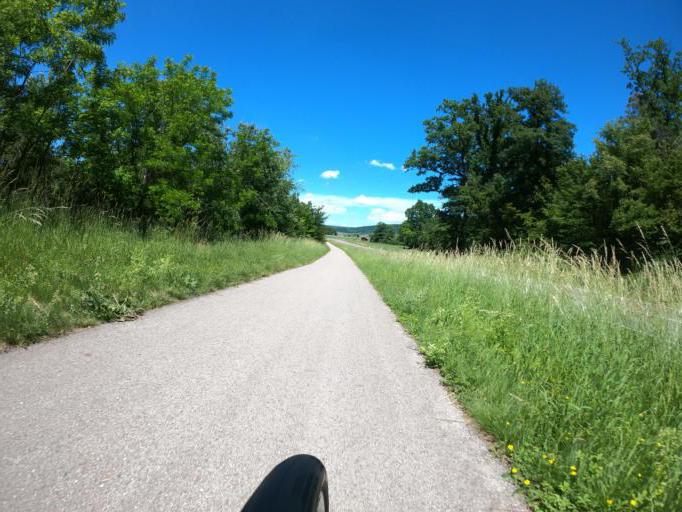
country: DE
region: Baden-Wuerttemberg
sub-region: Regierungsbezirk Stuttgart
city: Sersheim
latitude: 48.9812
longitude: 9.0231
